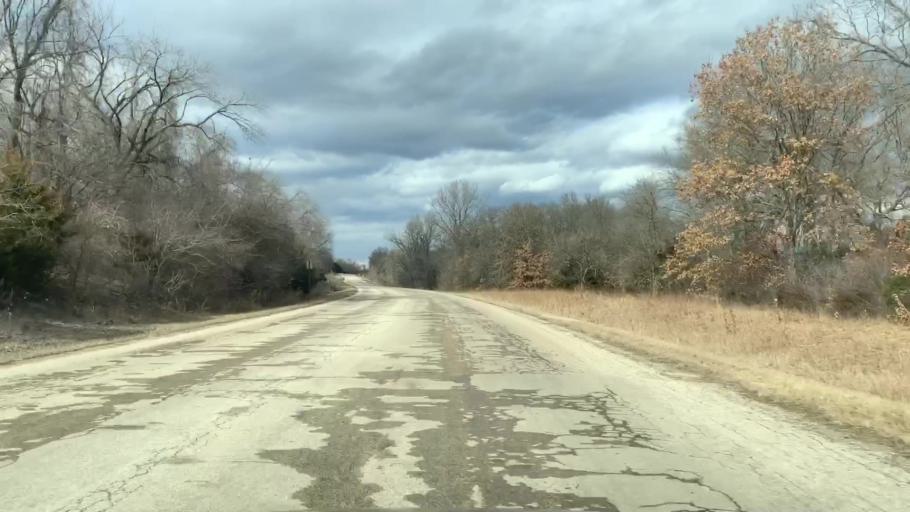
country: US
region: Kansas
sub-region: Allen County
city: Humboldt
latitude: 37.7497
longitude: -95.4703
